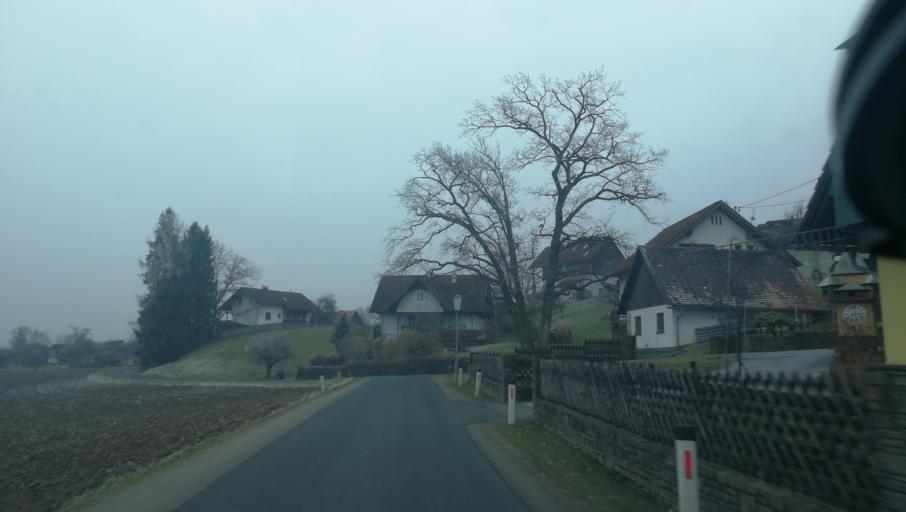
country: AT
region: Styria
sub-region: Politischer Bezirk Deutschlandsberg
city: Stainz
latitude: 46.8970
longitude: 15.2412
